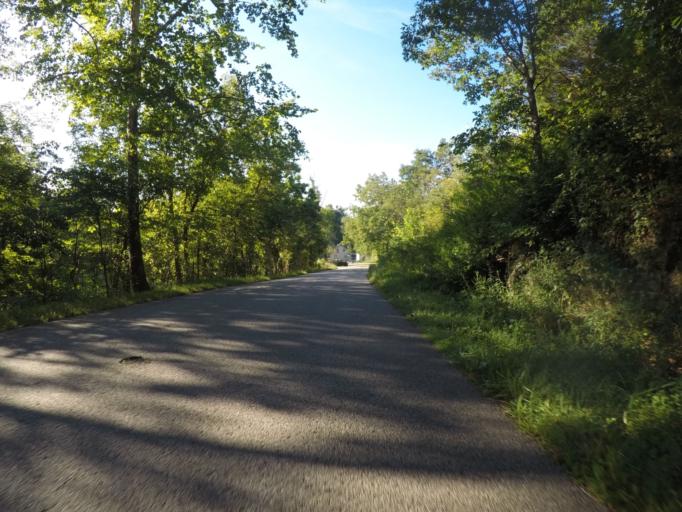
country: US
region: West Virginia
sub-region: Cabell County
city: Huntington
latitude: 38.5204
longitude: -82.5021
